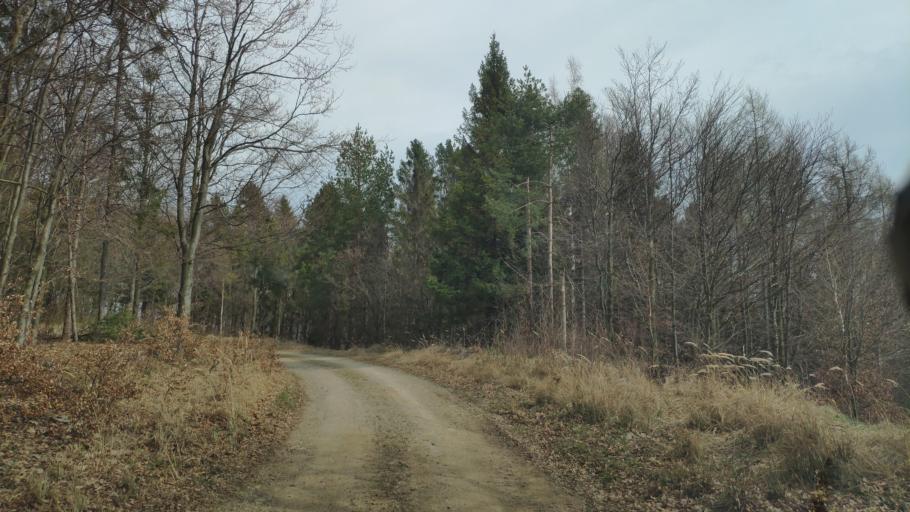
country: SK
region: Kosicky
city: Moldava nad Bodvou
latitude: 48.7405
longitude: 21.0444
